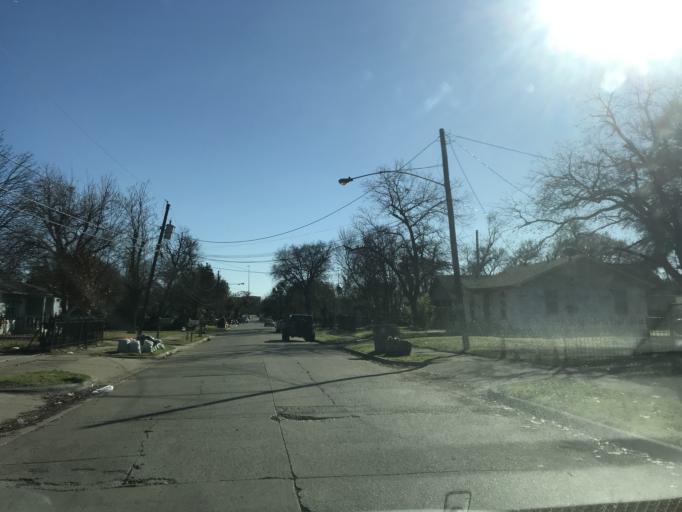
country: US
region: Texas
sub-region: Dallas County
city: Cockrell Hill
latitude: 32.7731
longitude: -96.9099
